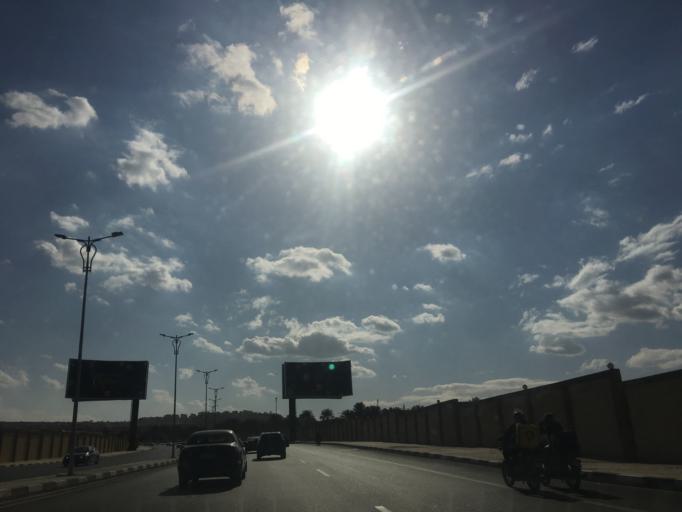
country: EG
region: Muhafazat al Qahirah
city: Cairo
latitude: 30.0393
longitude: 31.3069
